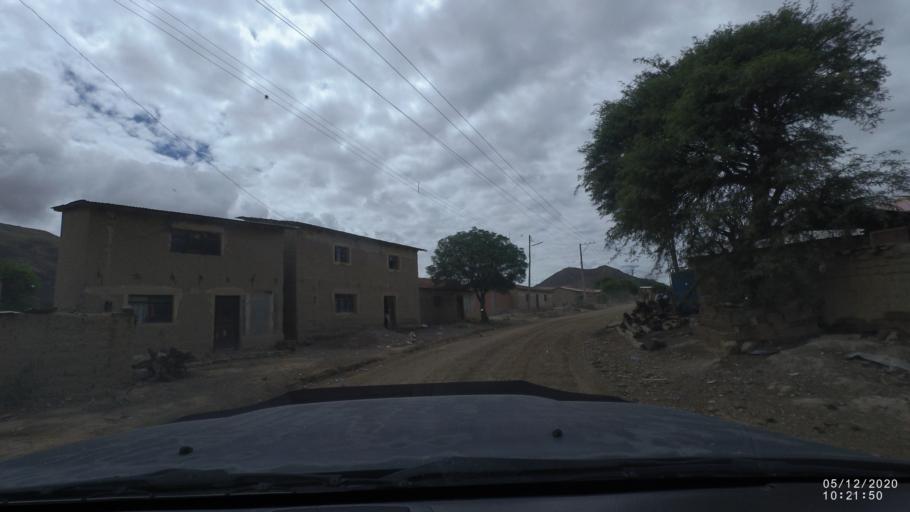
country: BO
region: Cochabamba
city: Sipe Sipe
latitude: -17.4921
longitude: -66.2823
